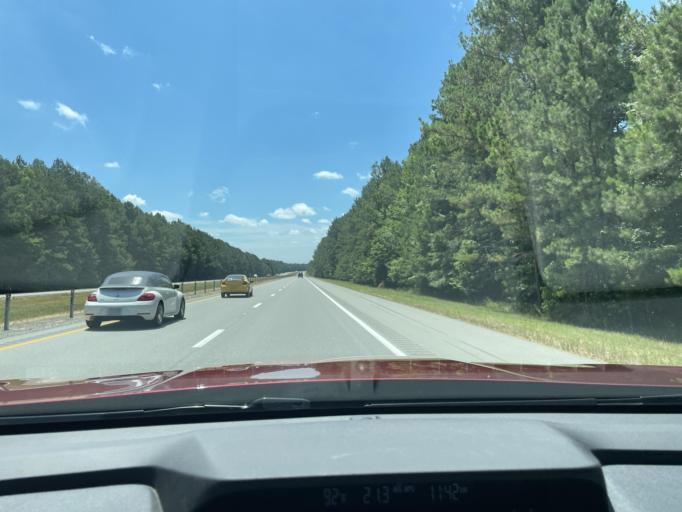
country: US
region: Arkansas
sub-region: Jefferson County
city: White Hall
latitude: 34.3318
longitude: -92.1612
